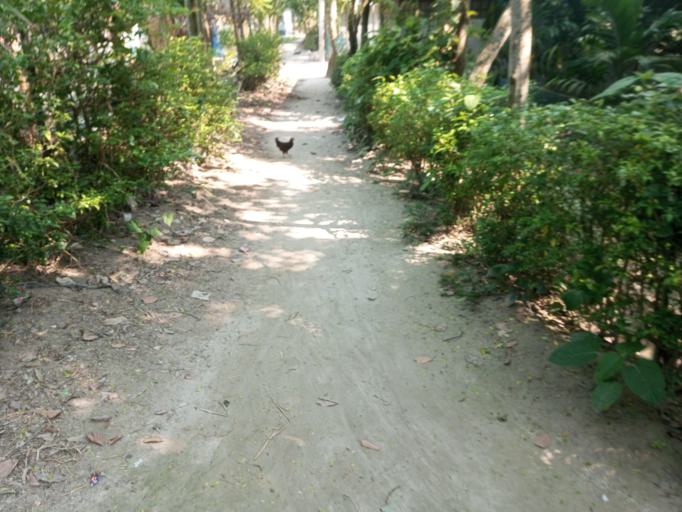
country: BD
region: Rangpur Division
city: Lalmanirhat
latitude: 25.9552
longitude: 89.2646
